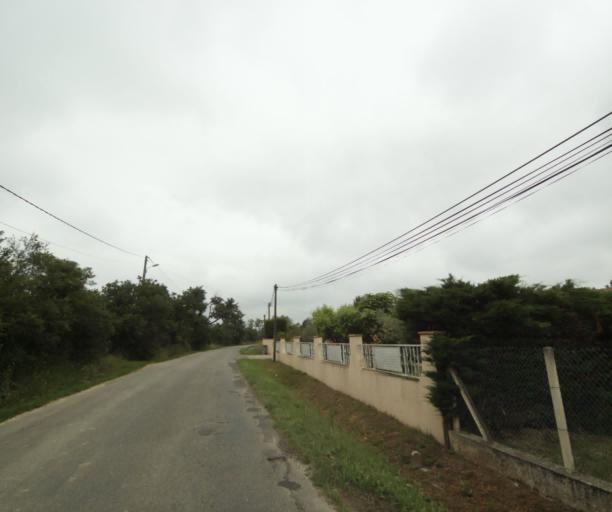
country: FR
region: Midi-Pyrenees
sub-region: Departement du Tarn-et-Garonne
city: Montbeton
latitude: 43.9902
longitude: 1.3071
